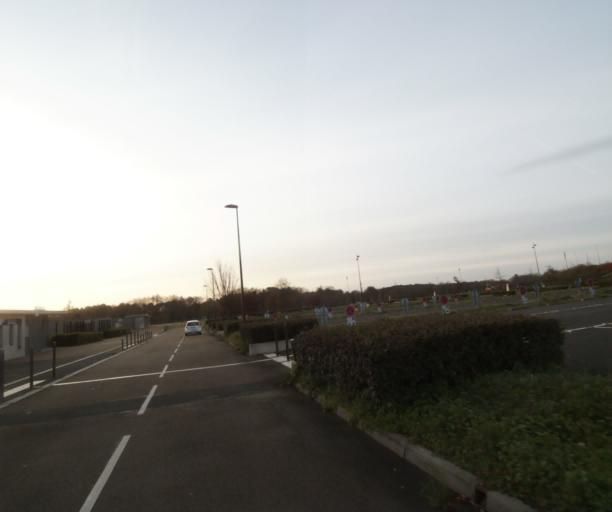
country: FR
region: Pays de la Loire
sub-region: Departement de la Sarthe
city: Le Mans
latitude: 47.9591
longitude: 0.2213
